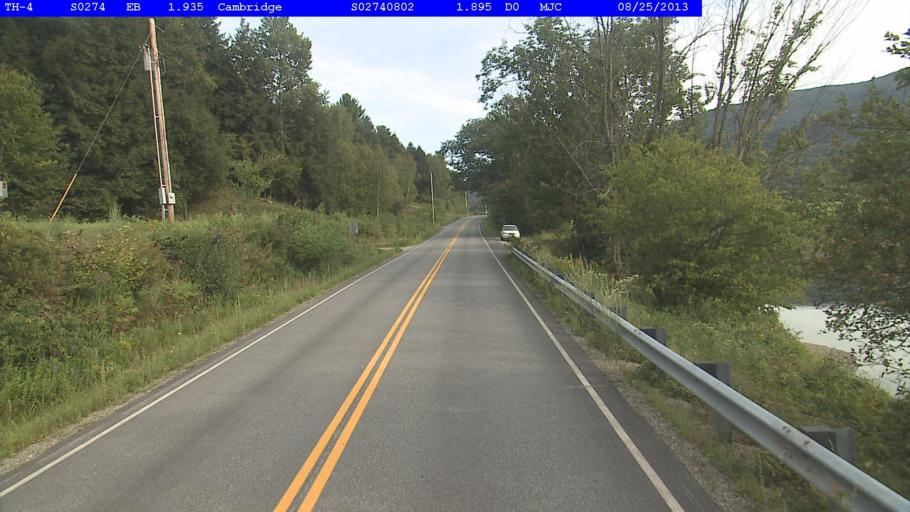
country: US
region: Vermont
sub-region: Lamoille County
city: Johnson
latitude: 44.6598
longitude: -72.7545
